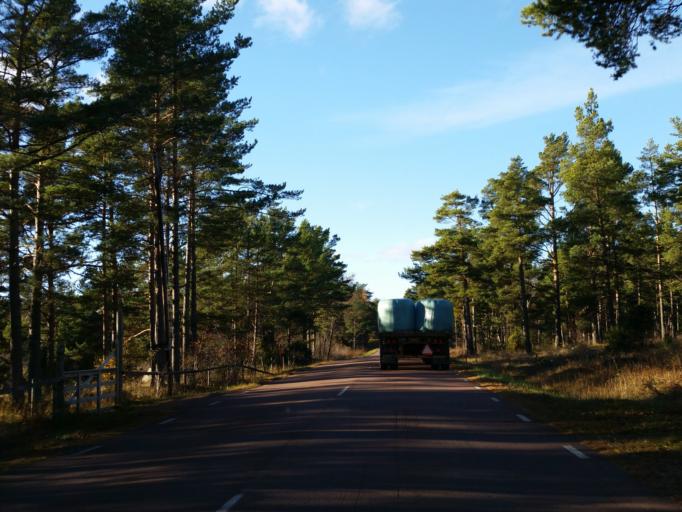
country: AX
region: Alands landsbygd
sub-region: Geta
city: Geta
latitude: 60.3649
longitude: 19.7862
